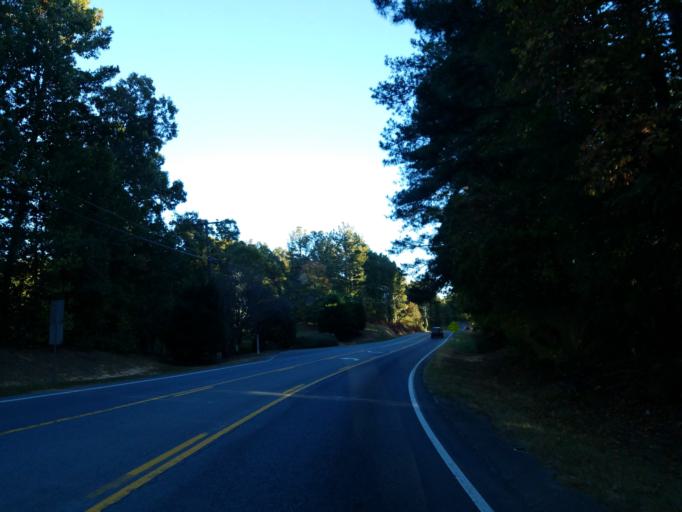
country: US
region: Georgia
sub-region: Dawson County
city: Dawsonville
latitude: 34.3774
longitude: -84.0477
